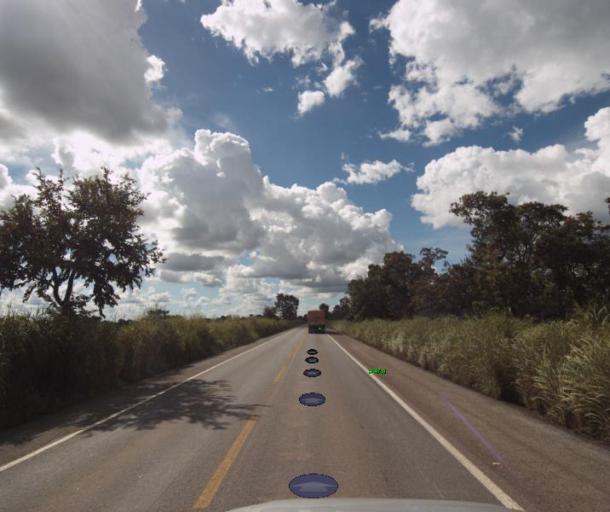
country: BR
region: Goias
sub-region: Porangatu
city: Porangatu
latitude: -13.2354
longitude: -49.1437
